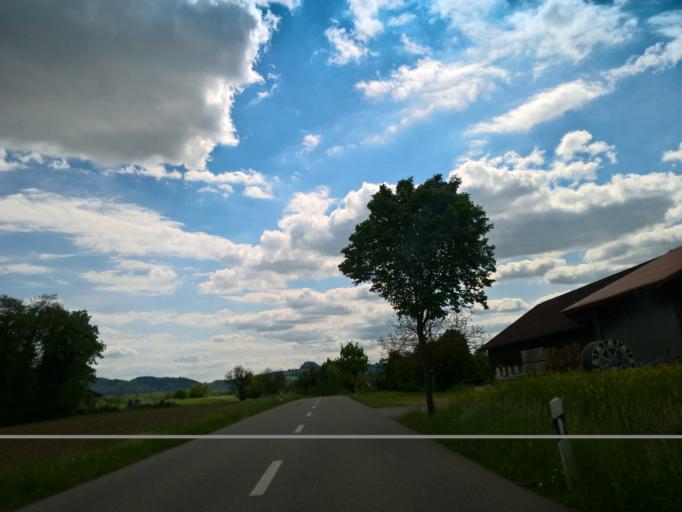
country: DE
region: Baden-Wuerttemberg
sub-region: Freiburg Region
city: Lottstetten
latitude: 47.6068
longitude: 8.6028
